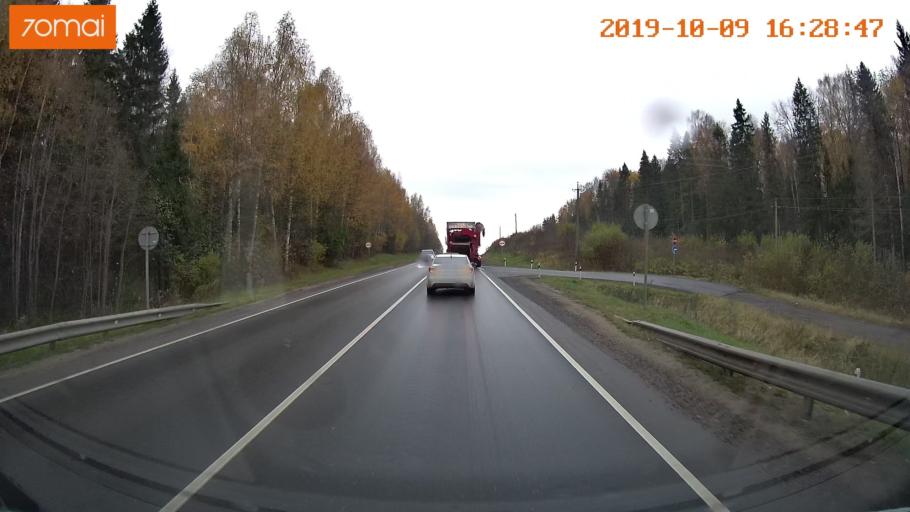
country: RU
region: Kostroma
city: Oktyabr'skiy
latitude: 57.6270
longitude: 40.9335
